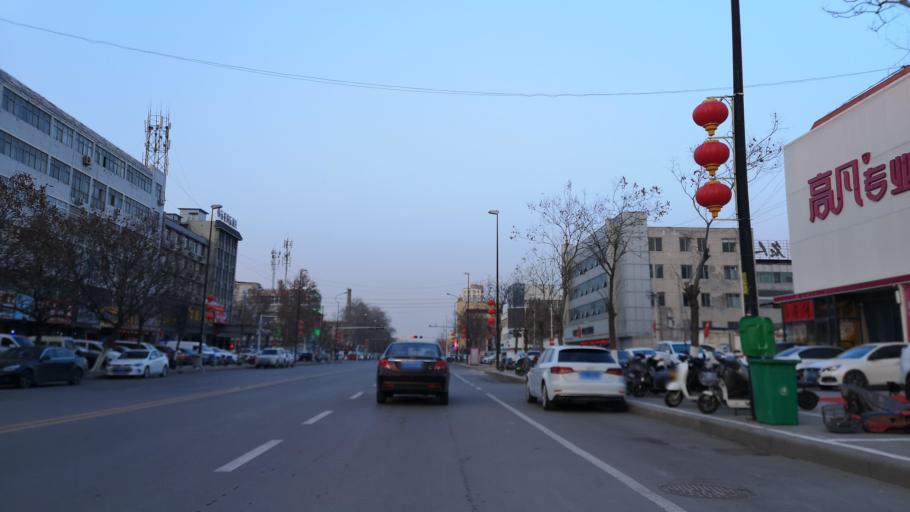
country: CN
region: Henan Sheng
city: Zhongyuanlu
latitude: 35.7768
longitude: 115.0602
